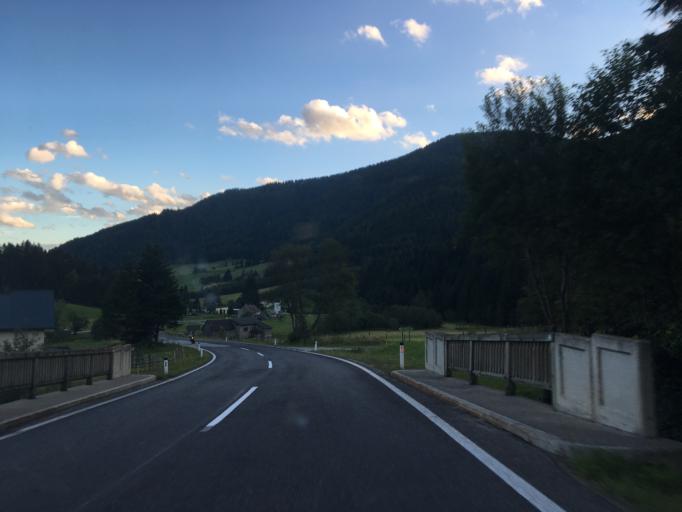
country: AT
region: Styria
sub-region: Politischer Bezirk Murtal
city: Sankt Johann am Tauern
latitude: 47.3792
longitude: 14.4626
